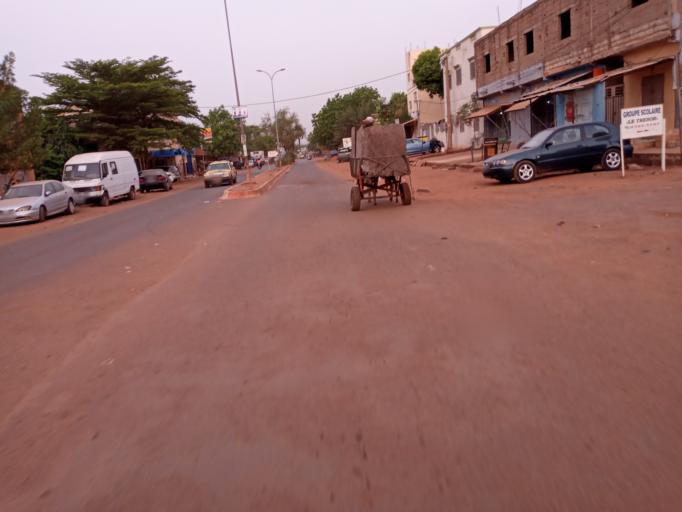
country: ML
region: Bamako
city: Bamako
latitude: 12.6625
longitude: -7.9752
